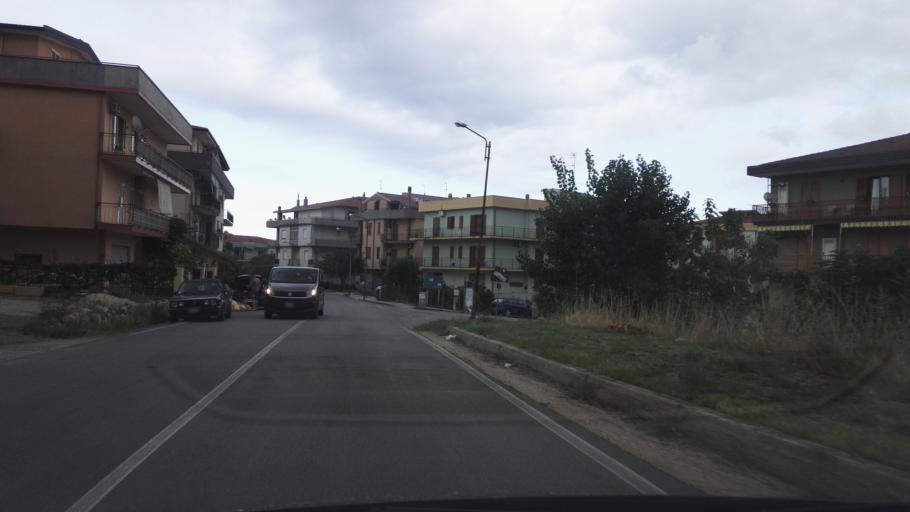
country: IT
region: Calabria
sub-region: Provincia di Catanzaro
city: Badolato Marina
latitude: 38.5709
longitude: 16.5622
